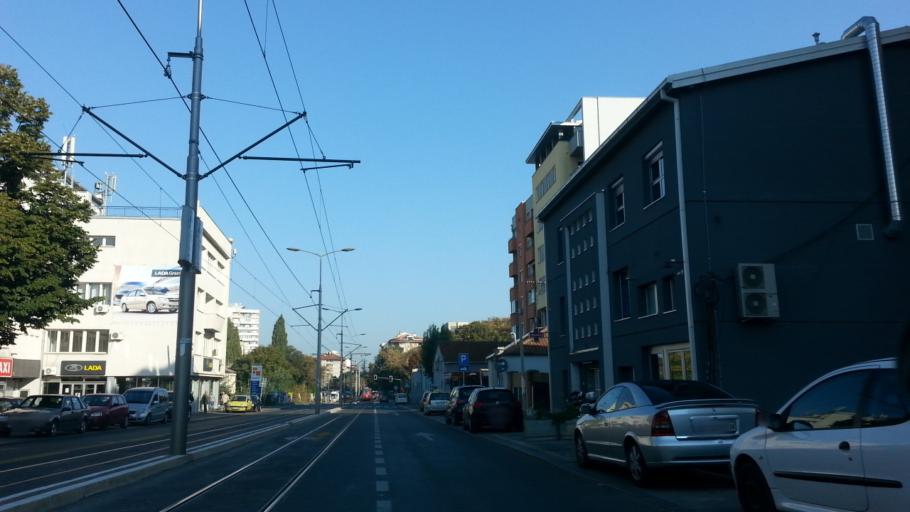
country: RS
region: Central Serbia
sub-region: Belgrade
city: Vozdovac
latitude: 44.7640
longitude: 20.4832
